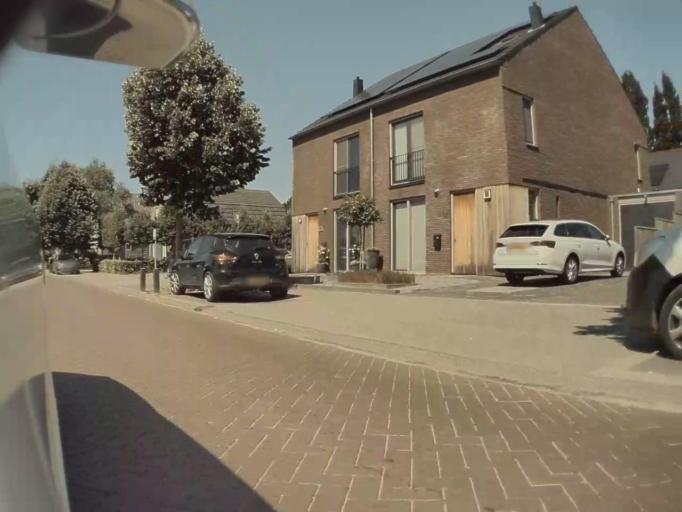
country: NL
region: North Brabant
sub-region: Gemeente 's-Hertogenbosch
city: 's-Hertogenbosch
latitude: 51.7162
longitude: 5.3655
